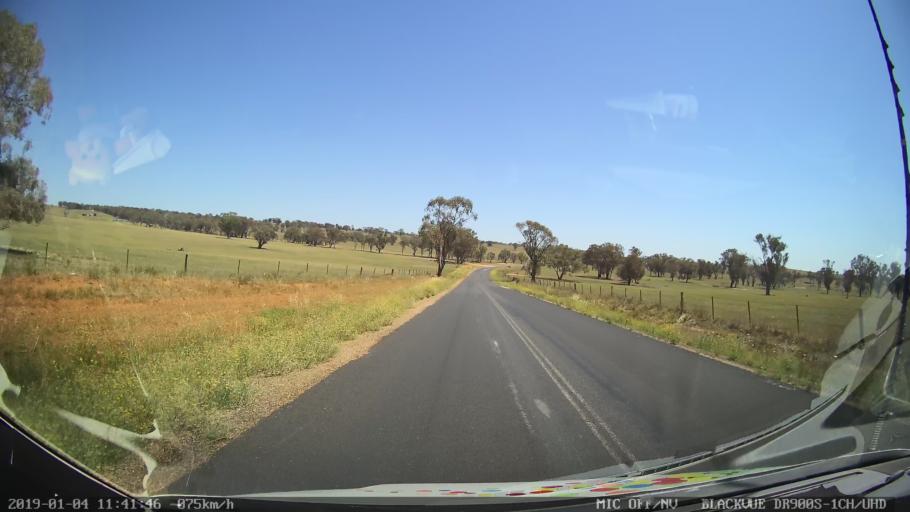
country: AU
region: New South Wales
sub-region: Cabonne
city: Molong
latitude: -32.9898
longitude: 148.7872
